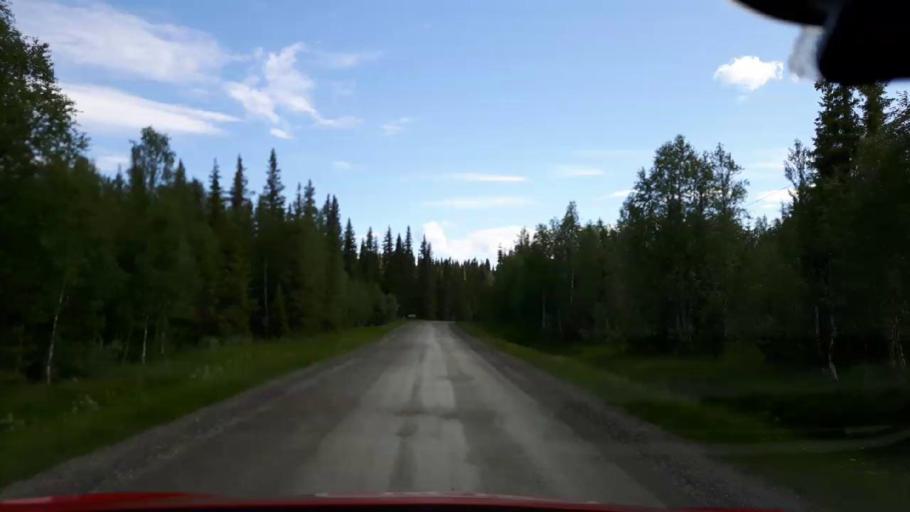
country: SE
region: Jaemtland
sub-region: Krokoms Kommun
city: Valla
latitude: 63.7855
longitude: 14.0487
